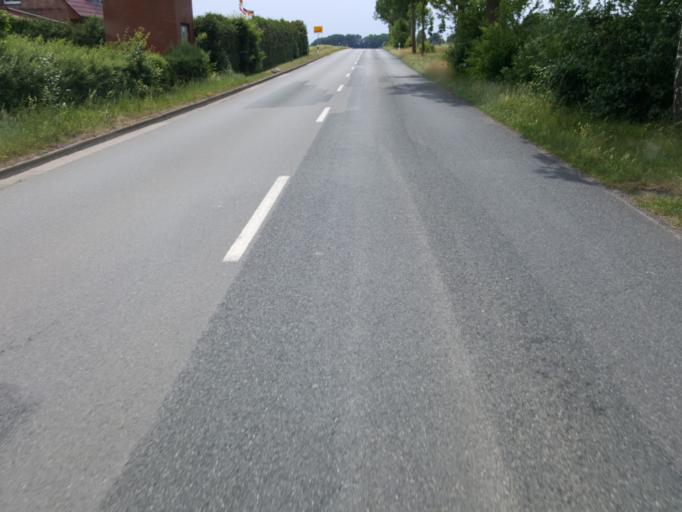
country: DE
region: Lower Saxony
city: Husum
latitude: 52.5875
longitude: 9.2491
